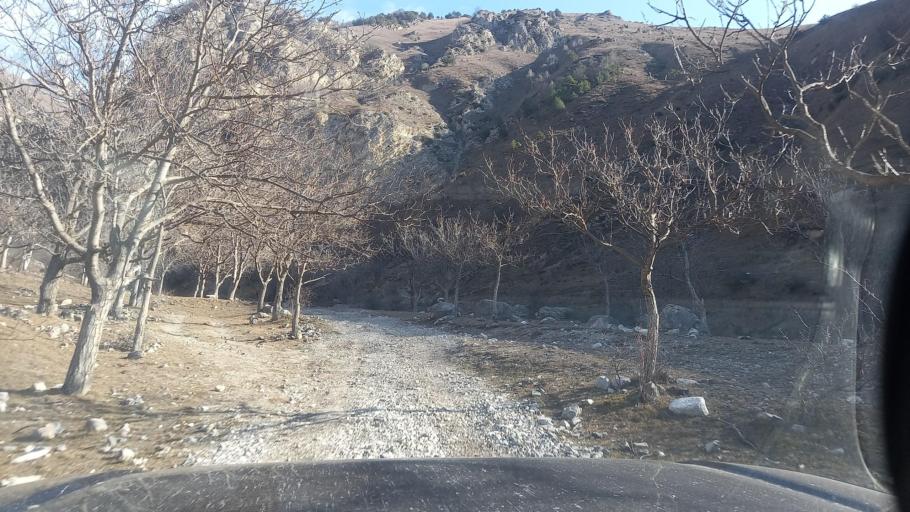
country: RU
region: Ingushetiya
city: Dzhayrakh
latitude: 42.8450
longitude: 44.6638
